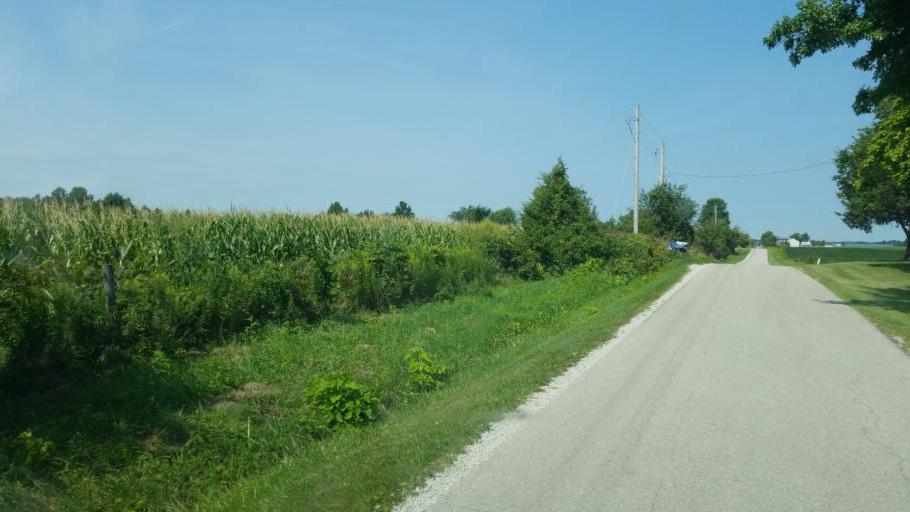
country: US
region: Ohio
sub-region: Crawford County
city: Bucyrus
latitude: 40.9023
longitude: -83.0741
